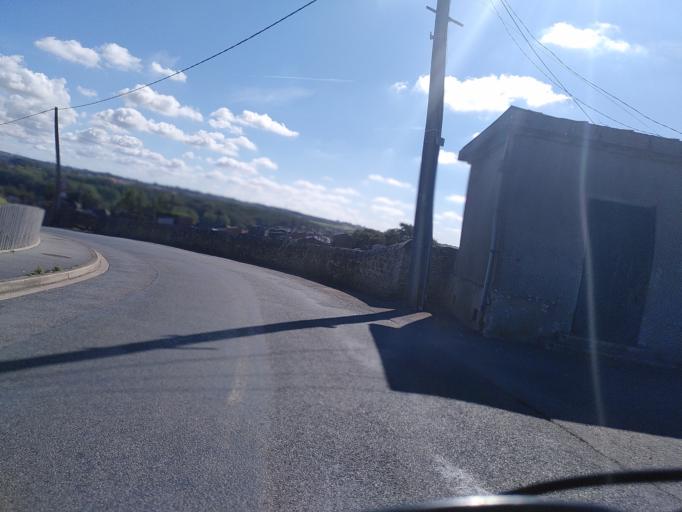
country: FR
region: Nord-Pas-de-Calais
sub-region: Departement du Pas-de-Calais
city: Wimille
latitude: 50.7700
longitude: 1.6280
